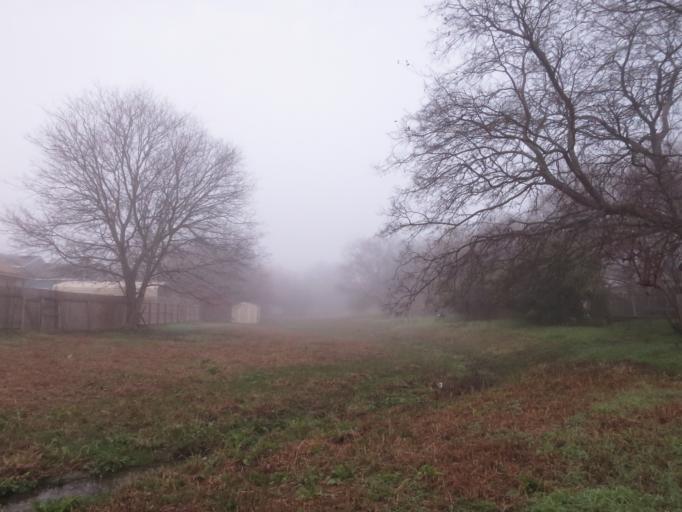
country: US
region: Texas
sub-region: Travis County
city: Wells Branch
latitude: 30.4209
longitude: -97.6857
